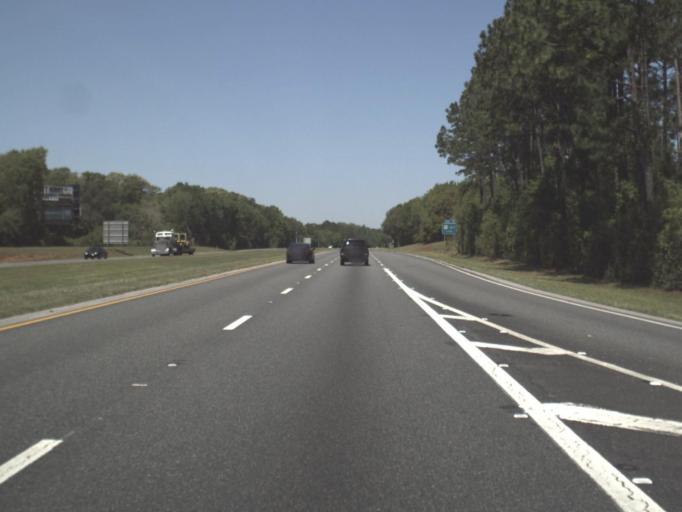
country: US
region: Florida
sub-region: Escambia County
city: Ensley
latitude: 30.5230
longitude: -87.3162
